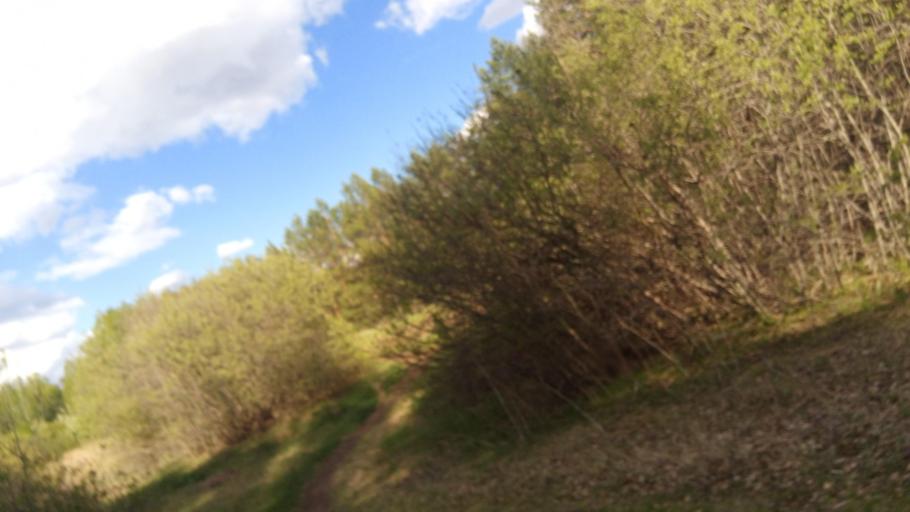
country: RU
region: Chelyabinsk
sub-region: Gorod Chelyabinsk
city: Chelyabinsk
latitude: 55.1577
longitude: 61.3210
